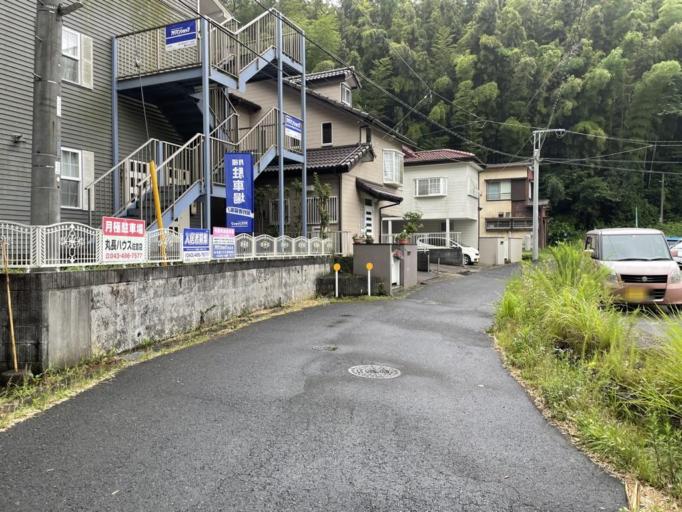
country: JP
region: Chiba
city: Sakura
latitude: 35.7231
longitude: 140.2276
